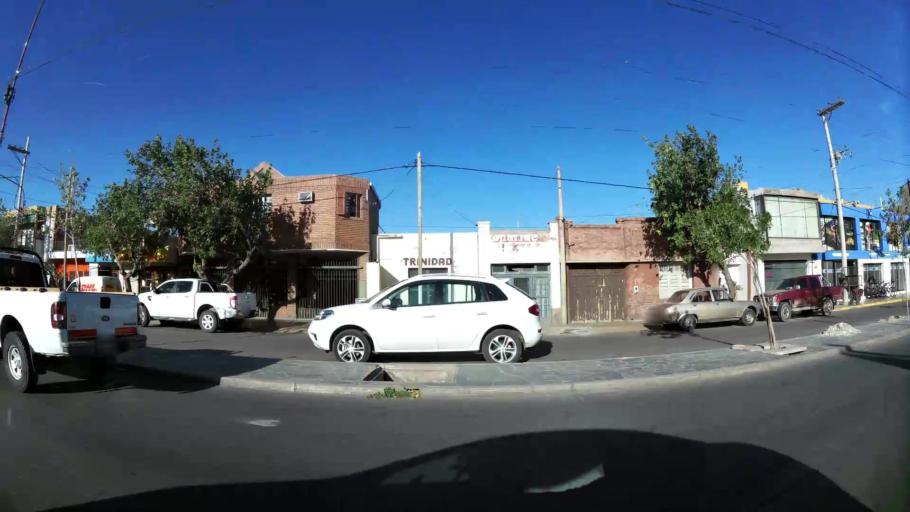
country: AR
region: San Juan
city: San Juan
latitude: -31.5451
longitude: -68.5205
